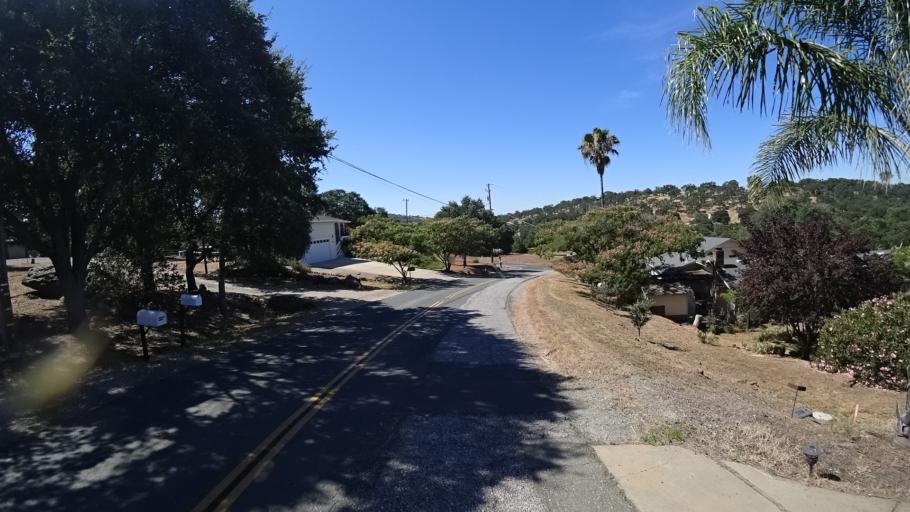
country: US
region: California
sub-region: Calaveras County
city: Rancho Calaveras
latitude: 38.1384
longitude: -120.8476
